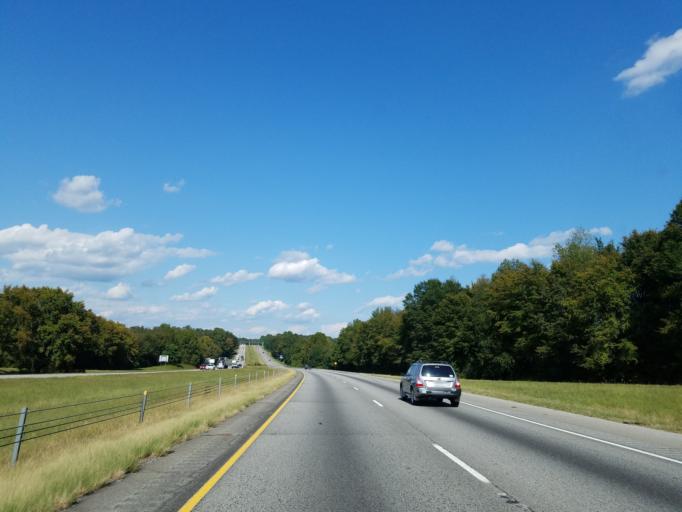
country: US
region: Georgia
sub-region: Franklin County
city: Carnesville
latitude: 34.3759
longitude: -83.2561
